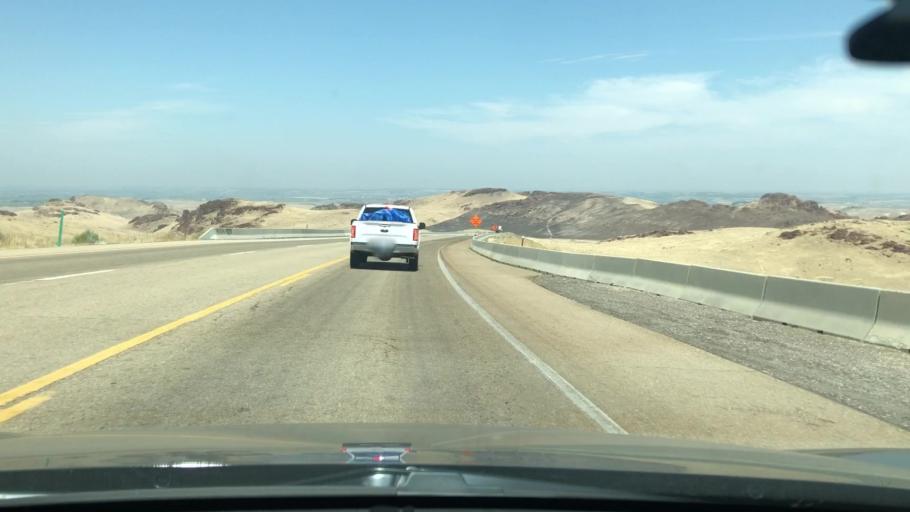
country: US
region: Idaho
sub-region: Owyhee County
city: Marsing
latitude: 43.4328
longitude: -116.8611
